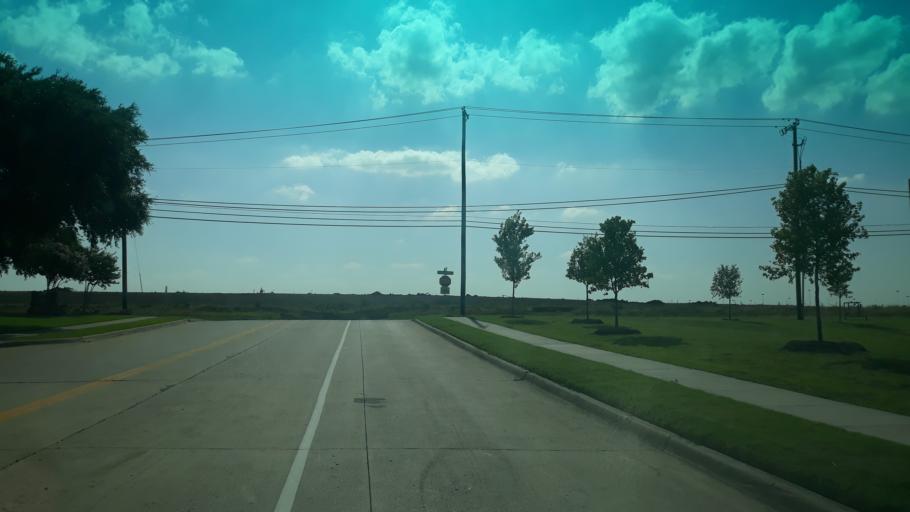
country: US
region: Texas
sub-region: Tarrant County
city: Euless
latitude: 32.8533
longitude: -97.0207
